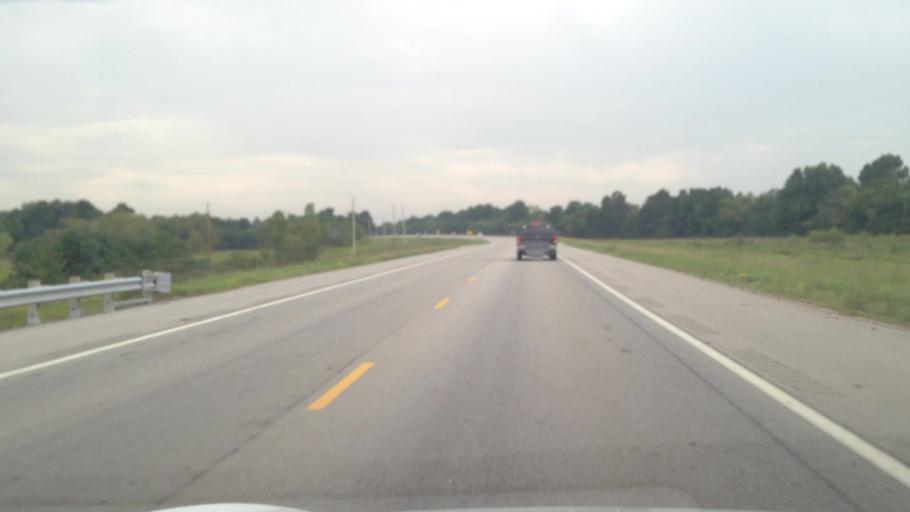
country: US
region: Kansas
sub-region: Cherokee County
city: Baxter Springs
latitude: 37.0620
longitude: -94.7305
